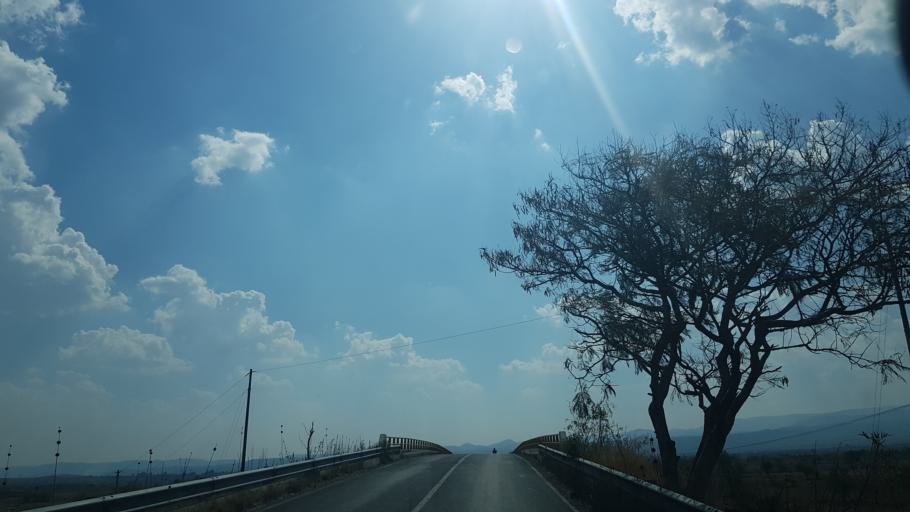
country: MX
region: Puebla
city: Atlixco
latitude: 18.9014
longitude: -98.4902
